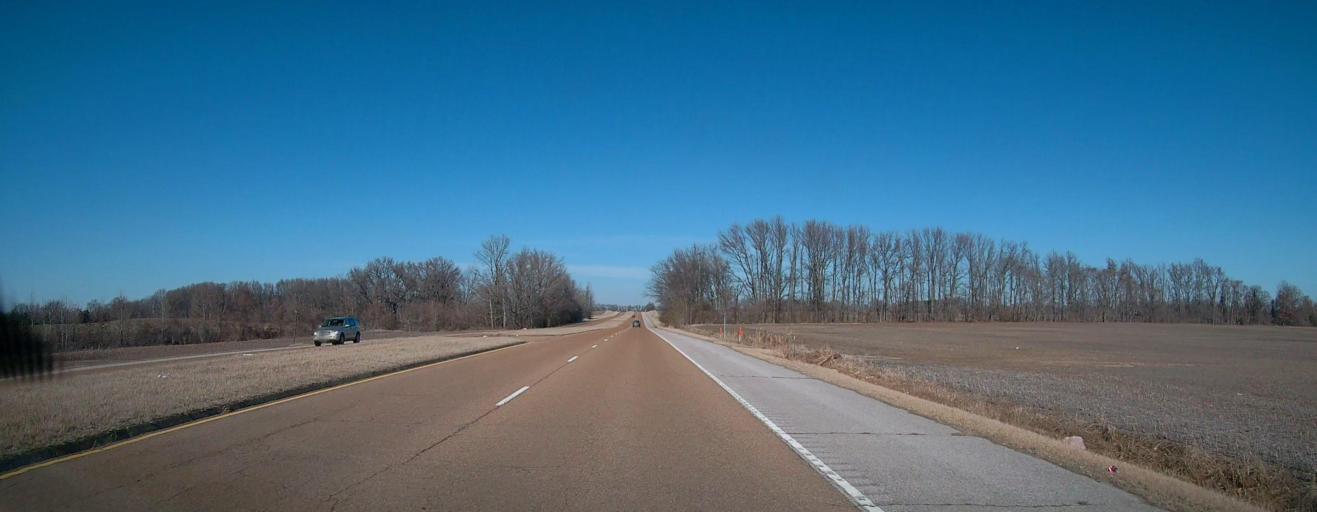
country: US
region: Tennessee
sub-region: Shelby County
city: Millington
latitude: 35.2964
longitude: -89.8821
